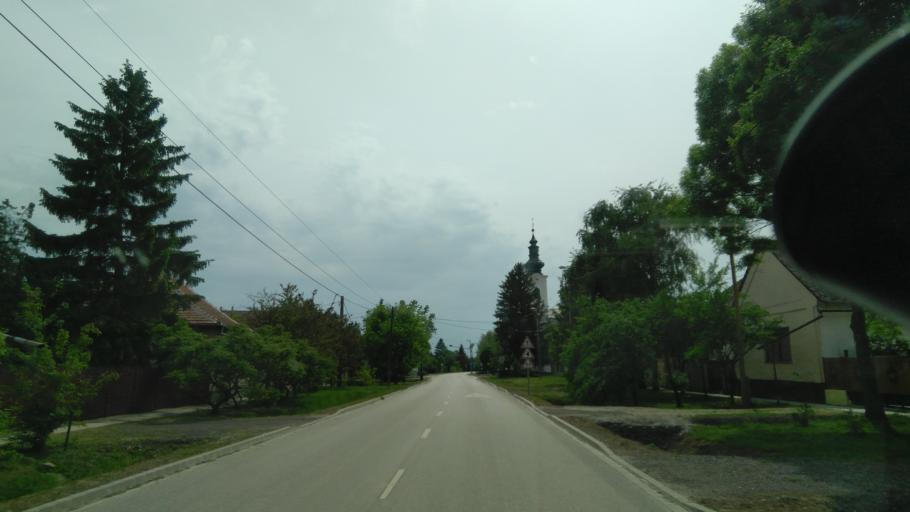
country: HU
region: Bekes
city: Mehkerek
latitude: 46.8702
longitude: 21.5238
